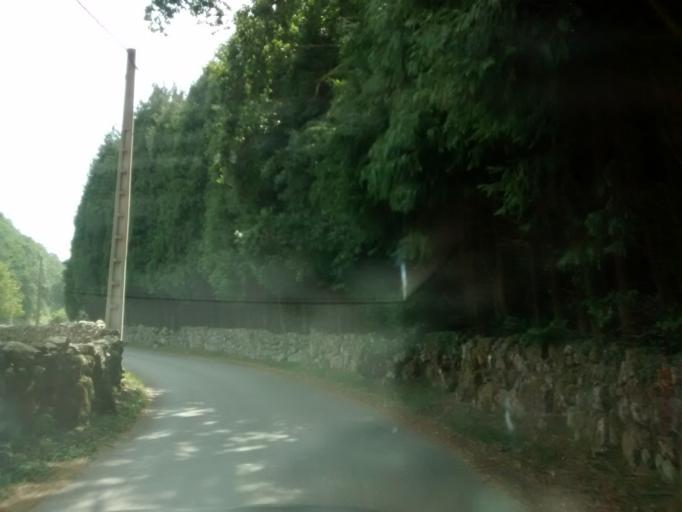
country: ES
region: Cantabria
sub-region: Provincia de Cantabria
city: Ruente
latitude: 43.2450
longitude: -4.2390
